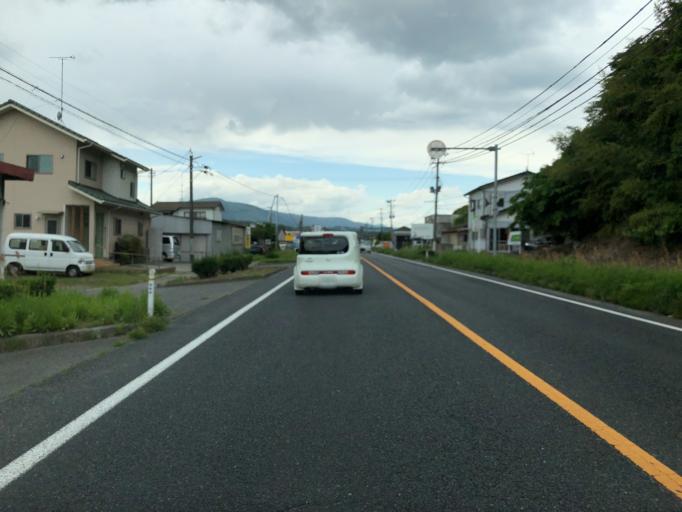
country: JP
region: Fukushima
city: Iwaki
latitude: 36.9909
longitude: 140.8655
